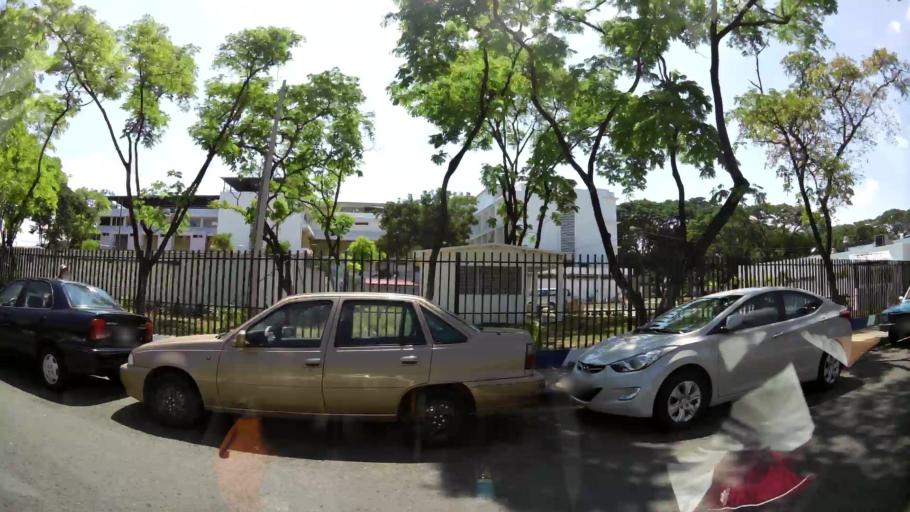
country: EC
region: Guayas
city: Guayaquil
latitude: -2.2345
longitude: -79.8984
